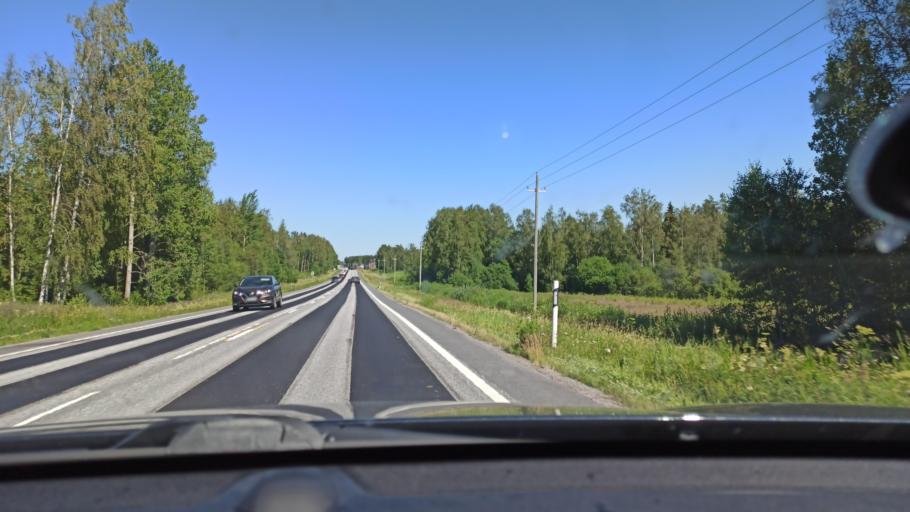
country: FI
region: Ostrobothnia
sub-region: Vaasa
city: Voera
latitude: 63.2071
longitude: 22.1532
